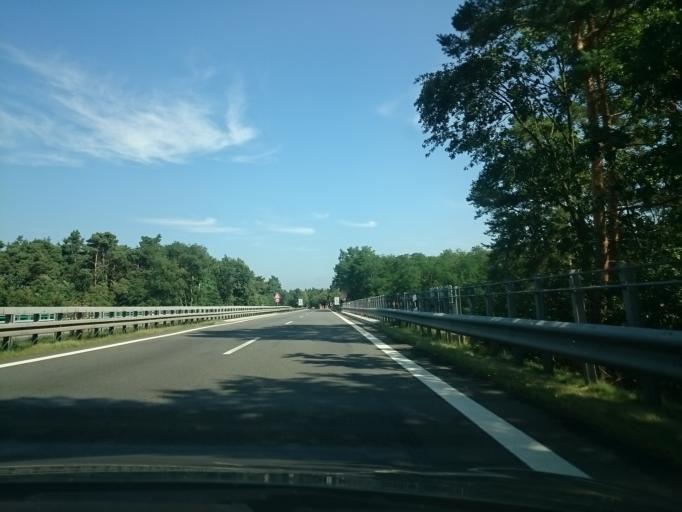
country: DE
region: Brandenburg
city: Lubbenau
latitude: 51.8437
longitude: 13.9240
